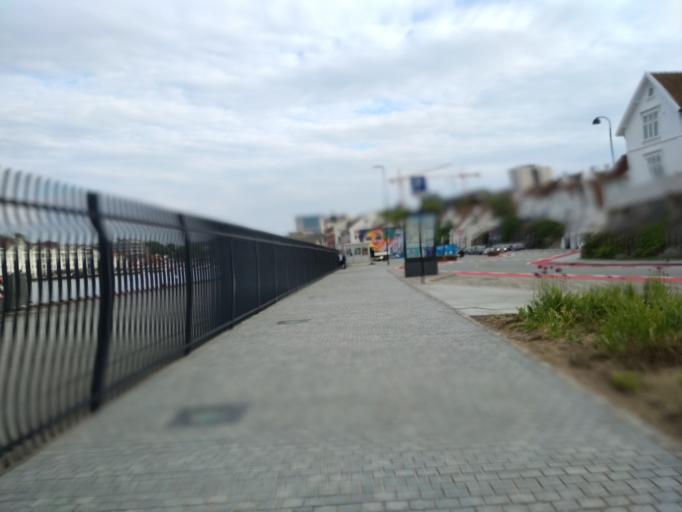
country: NO
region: Rogaland
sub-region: Stavanger
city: Stavanger
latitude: 58.9741
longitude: 5.7257
